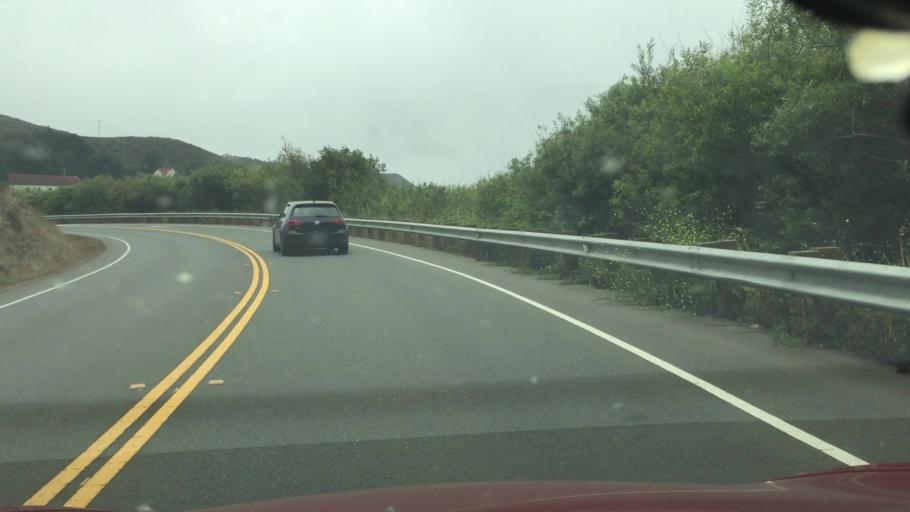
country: US
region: California
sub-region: Marin County
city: Marin City
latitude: 37.8331
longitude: -122.5223
